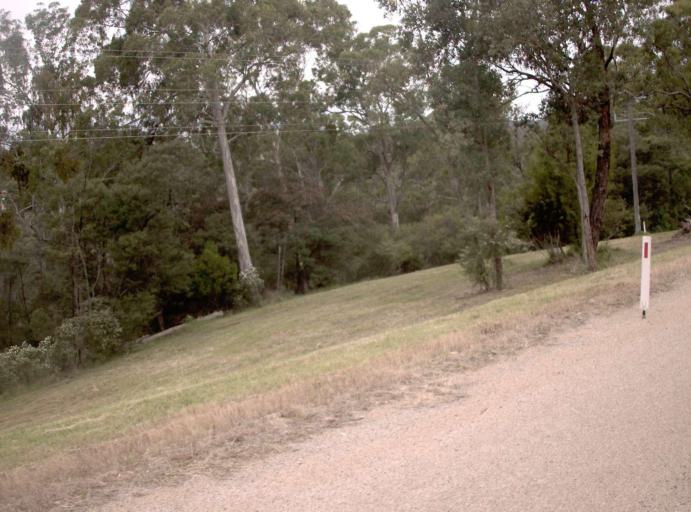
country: AU
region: Victoria
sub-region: East Gippsland
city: Lakes Entrance
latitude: -37.7258
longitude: 148.0880
